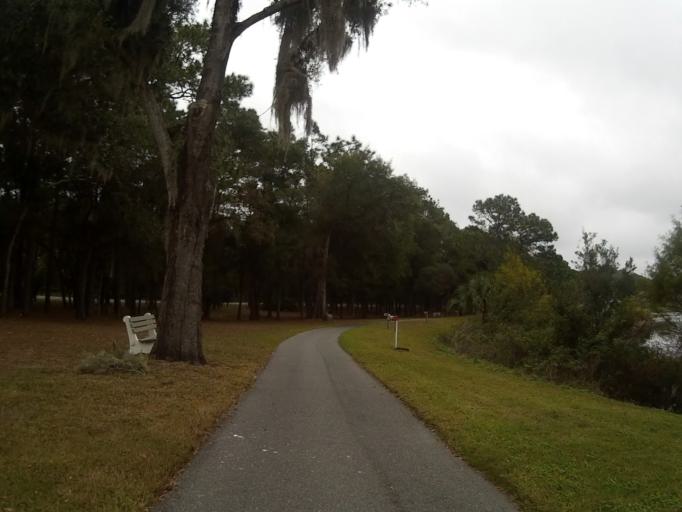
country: US
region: Florida
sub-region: Lake County
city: Umatilla
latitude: 28.9667
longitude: -81.6579
